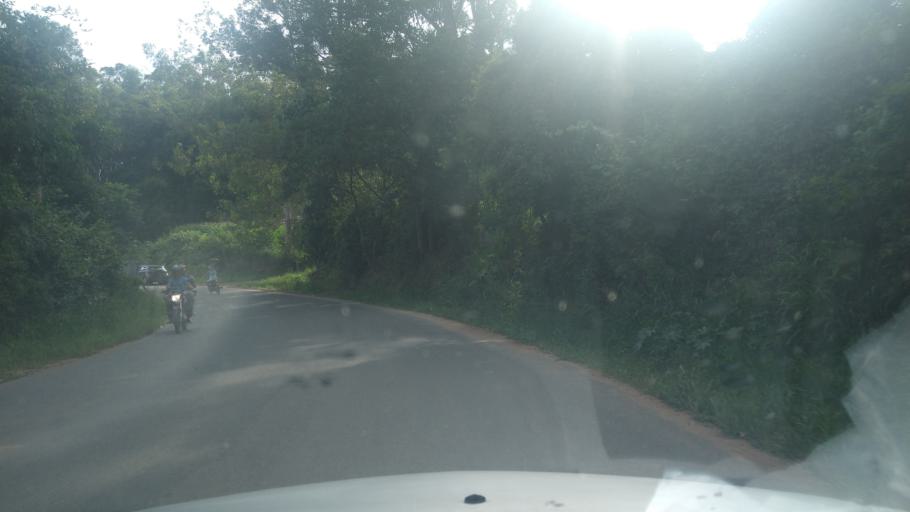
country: BR
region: Minas Gerais
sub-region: Extrema
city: Extrema
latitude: -22.7363
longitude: -46.3691
